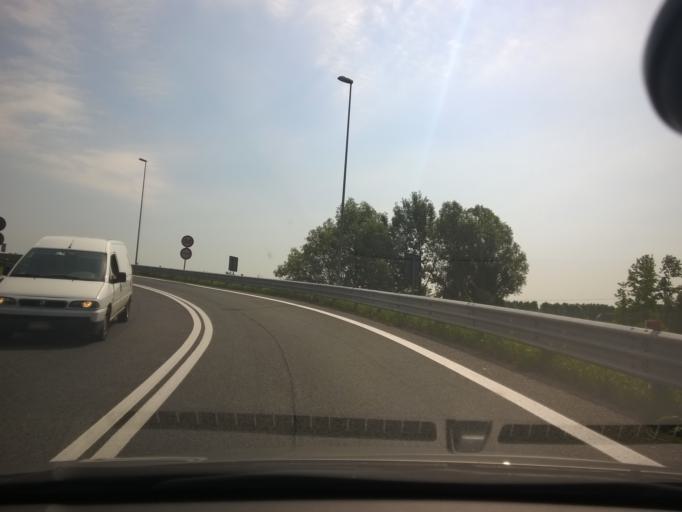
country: IT
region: Friuli Venezia Giulia
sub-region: Provincia di Pordenone
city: Tamai
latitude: 45.9453
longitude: 12.5771
